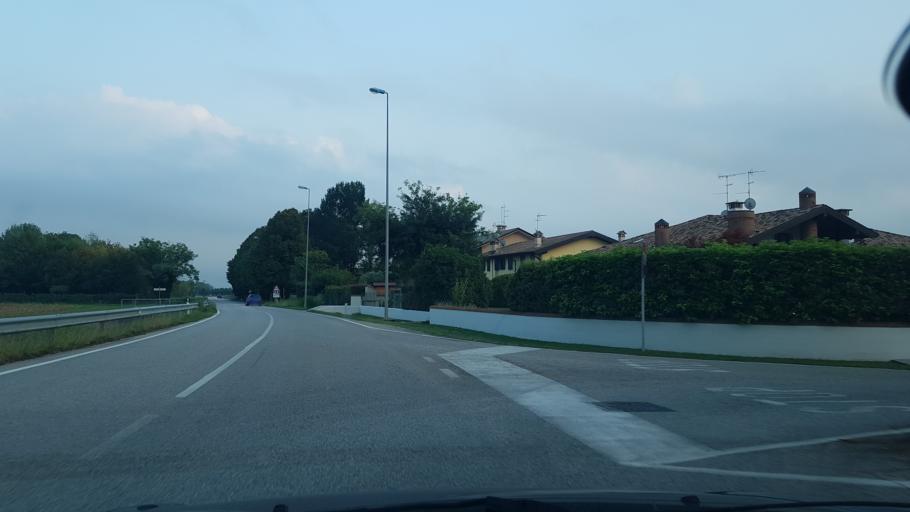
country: IT
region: Friuli Venezia Giulia
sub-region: Provincia di Udine
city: Trivignano Udinese
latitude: 45.9496
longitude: 13.3421
